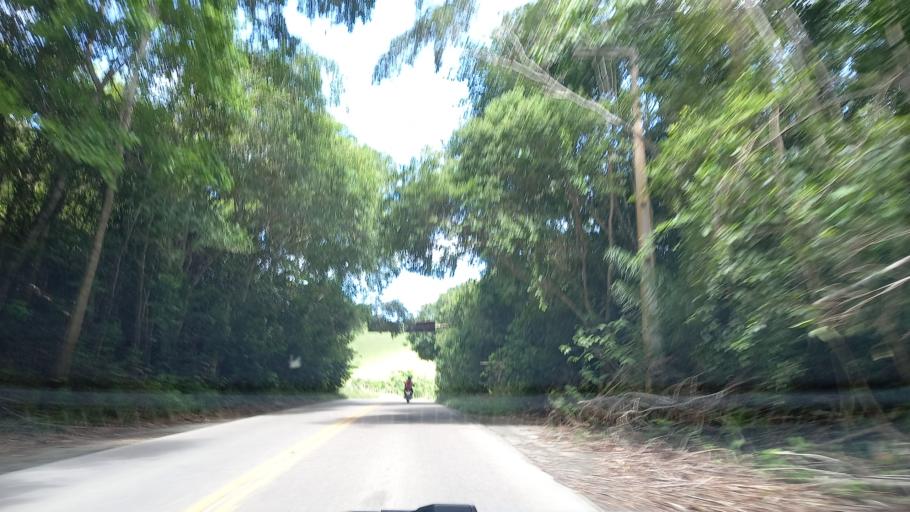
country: BR
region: Pernambuco
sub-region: Rio Formoso
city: Rio Formoso
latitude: -8.7376
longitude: -35.1721
